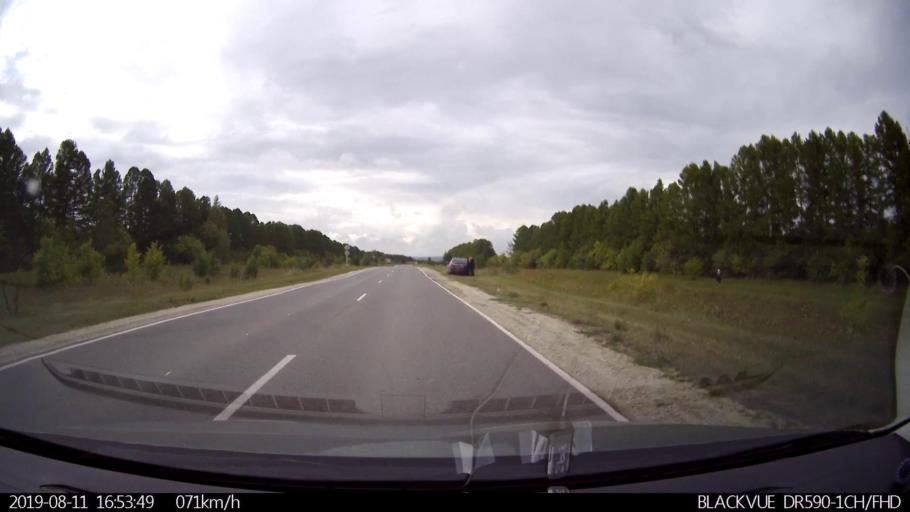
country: RU
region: Ulyanovsk
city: Mayna
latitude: 54.2666
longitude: 47.6687
